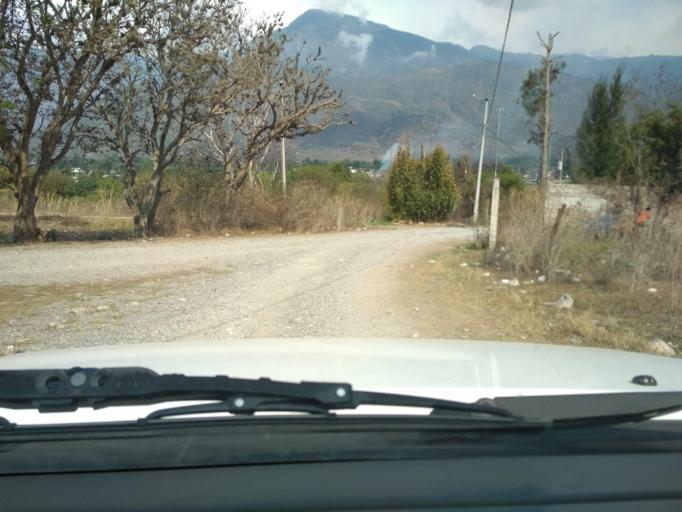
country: MX
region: Veracruz
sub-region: Acultzingo
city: Sierra de Agua
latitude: 18.7688
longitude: -97.2299
